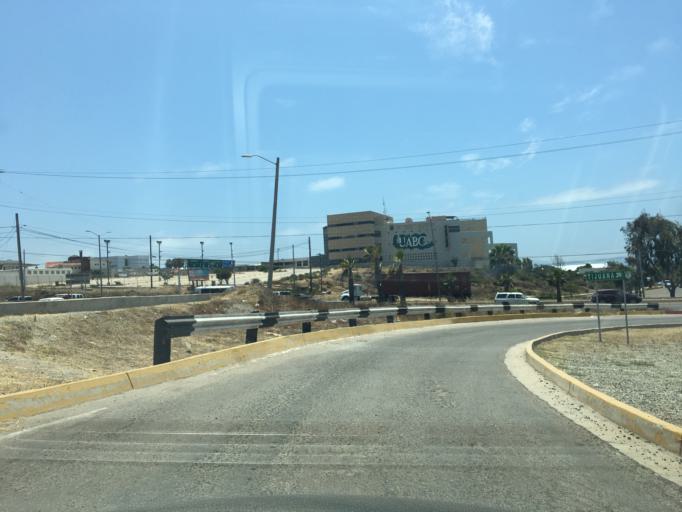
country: MX
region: Baja California
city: El Sauzal
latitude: 31.8673
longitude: -116.6671
